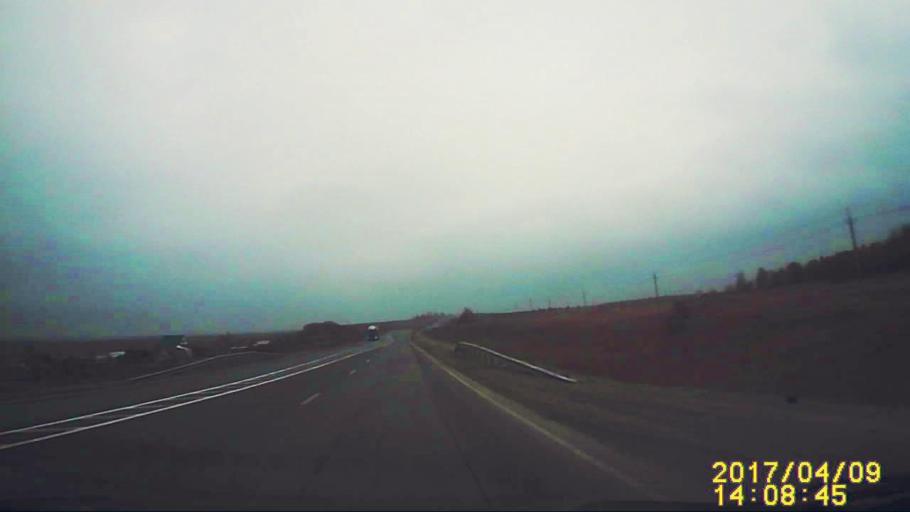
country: RU
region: Ulyanovsk
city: Silikatnyy
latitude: 54.0225
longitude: 48.2147
